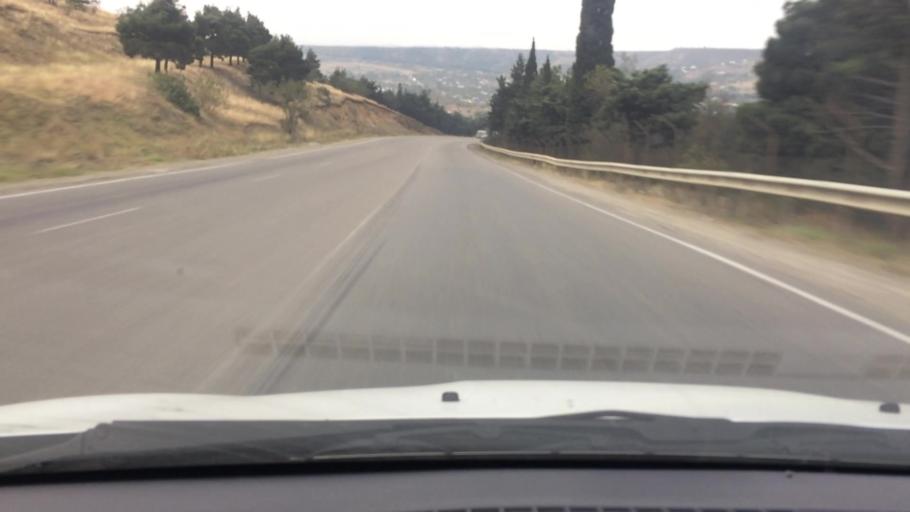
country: GE
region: T'bilisi
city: Tbilisi
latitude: 41.6233
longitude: 44.8016
